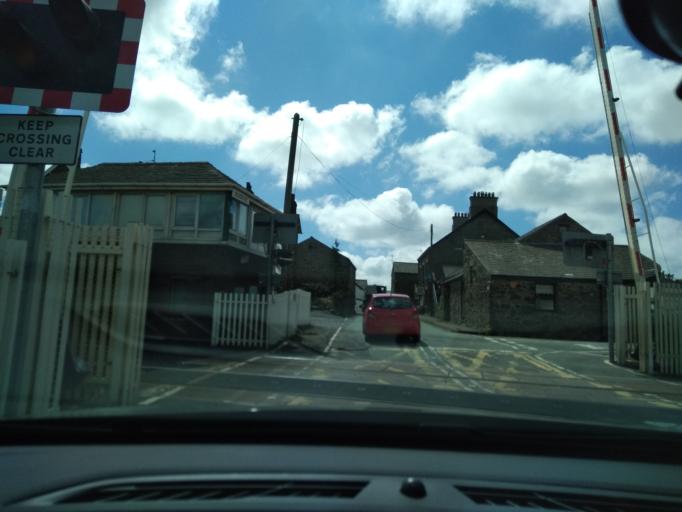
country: GB
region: England
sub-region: Cumbria
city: Millom
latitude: 54.2259
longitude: -3.3342
